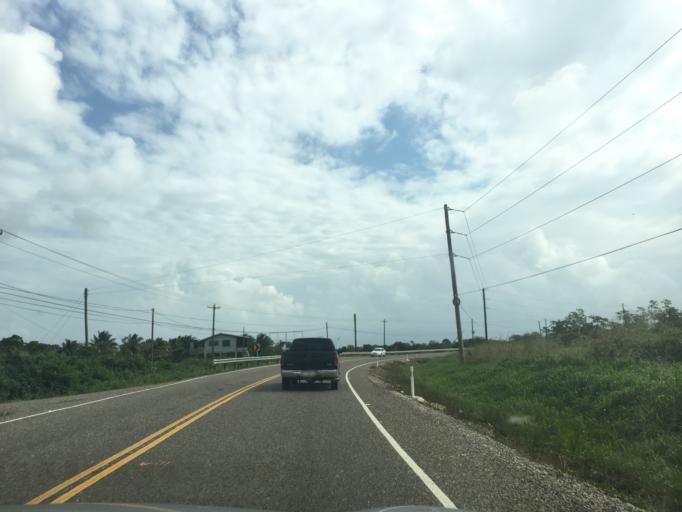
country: BZ
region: Stann Creek
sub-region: Dangriga
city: Dangriga
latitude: 17.0024
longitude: -88.3043
